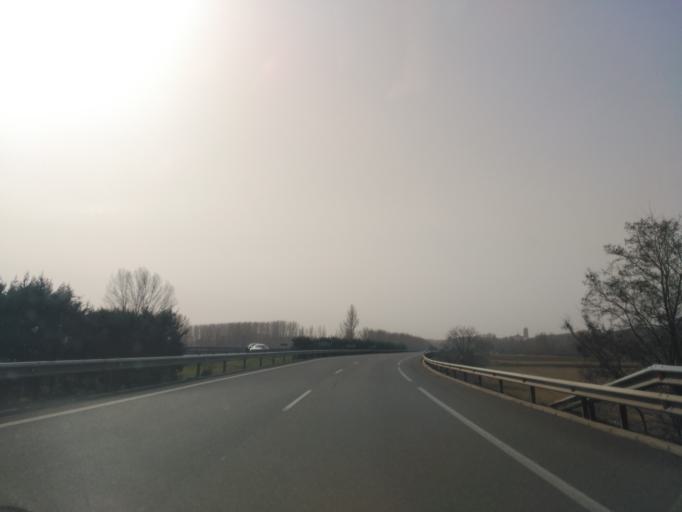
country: ES
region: Castille and Leon
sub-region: Provincia de Palencia
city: Duenas
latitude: 41.8880
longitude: -4.5310
